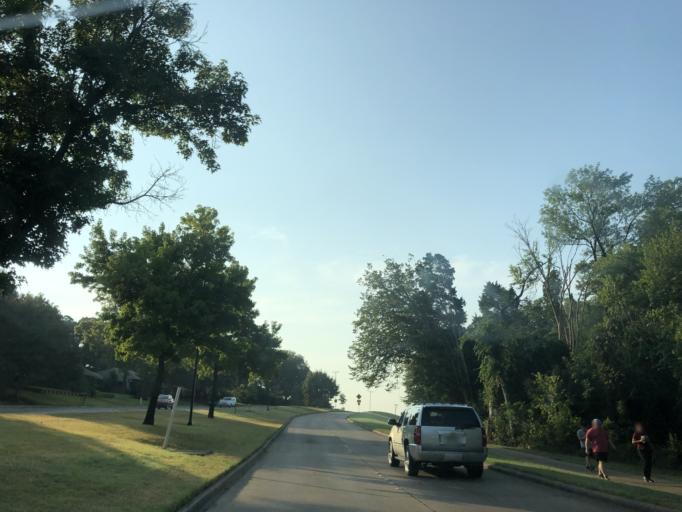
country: US
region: Texas
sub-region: Dallas County
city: Garland
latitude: 32.8541
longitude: -96.6134
